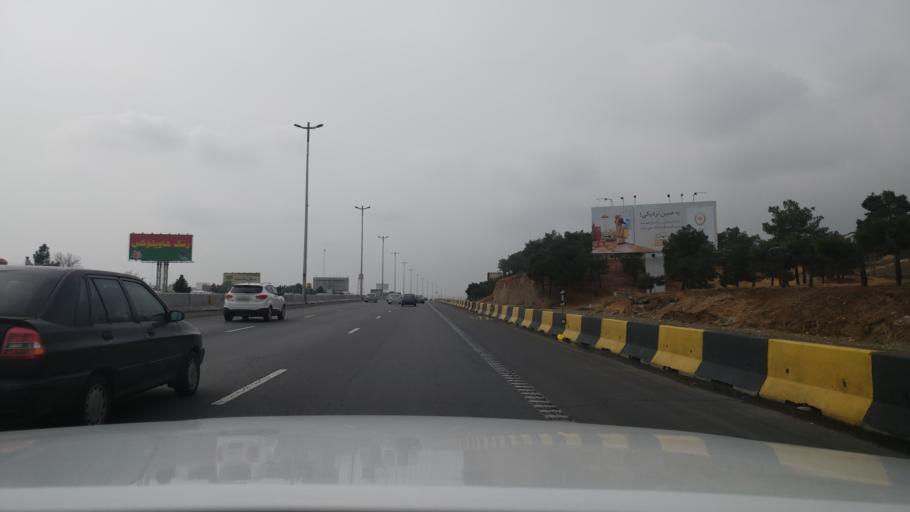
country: IR
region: Tehran
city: Shahr-e Qods
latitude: 35.7180
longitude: 51.2268
